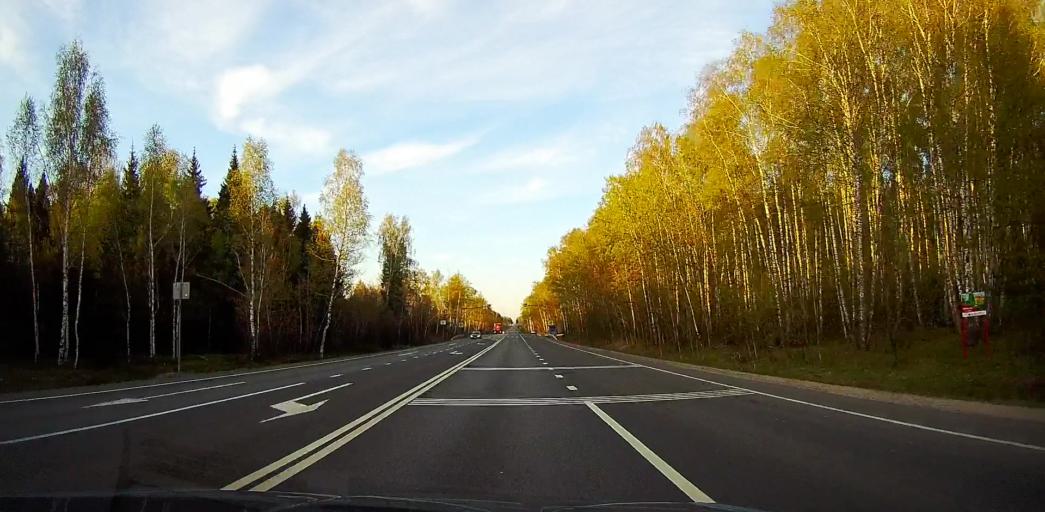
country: RU
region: Moskovskaya
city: Meshcherino
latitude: 55.2348
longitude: 38.4193
